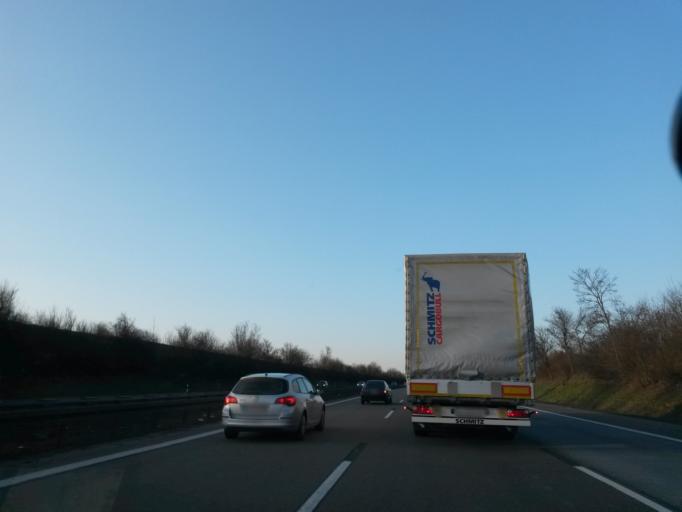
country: DE
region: Bavaria
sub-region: Upper Bavaria
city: Stammham
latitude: 48.8537
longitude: 11.4649
